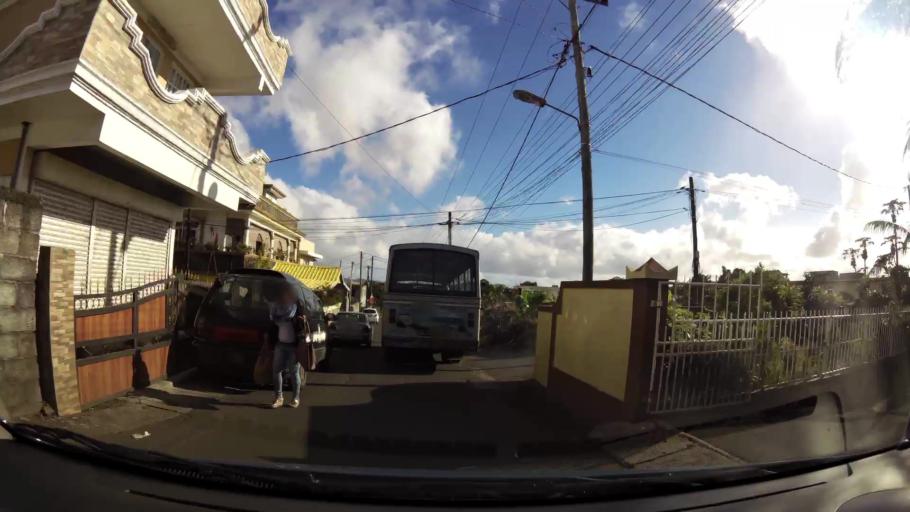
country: MU
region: Plaines Wilhems
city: Curepipe
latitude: -20.3249
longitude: 57.5072
